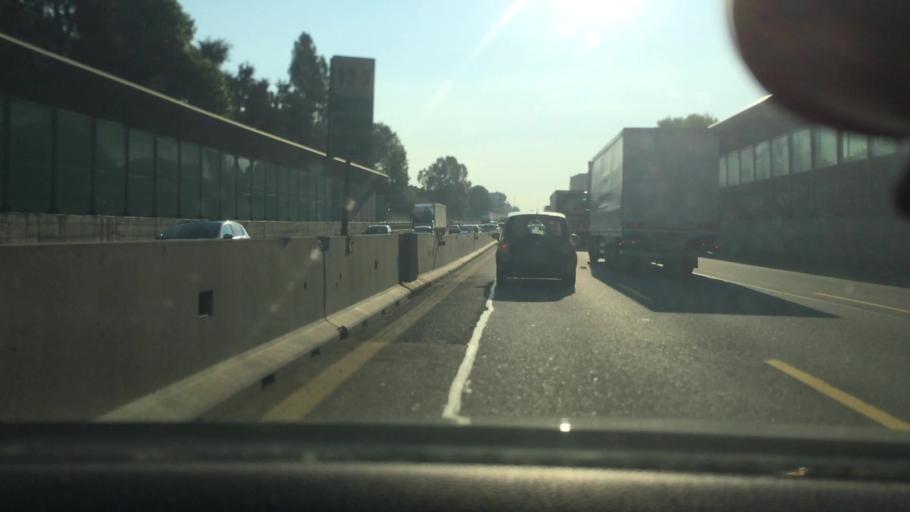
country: IT
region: Lombardy
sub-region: Citta metropolitana di Milano
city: Cinisello Balsamo
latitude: 45.5492
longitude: 9.2271
